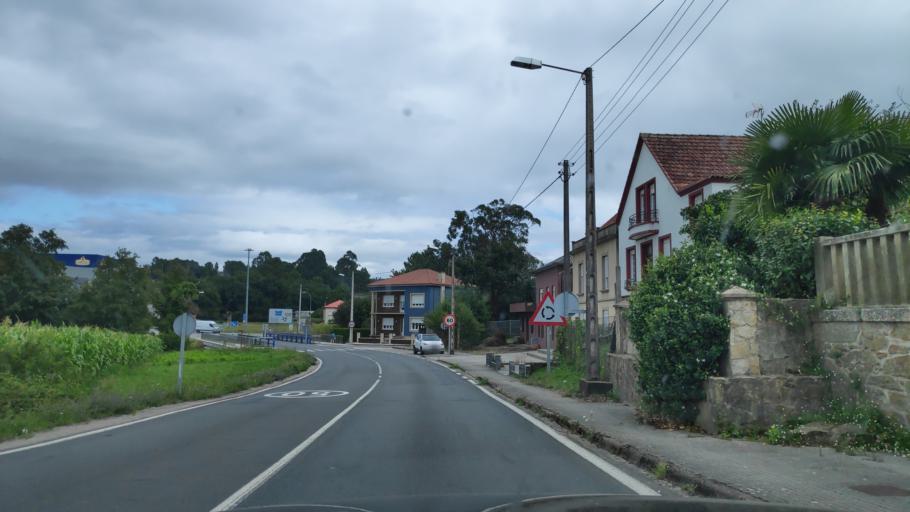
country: ES
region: Galicia
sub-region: Provincia da Coruna
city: Rianxo
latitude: 42.6695
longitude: -8.8138
